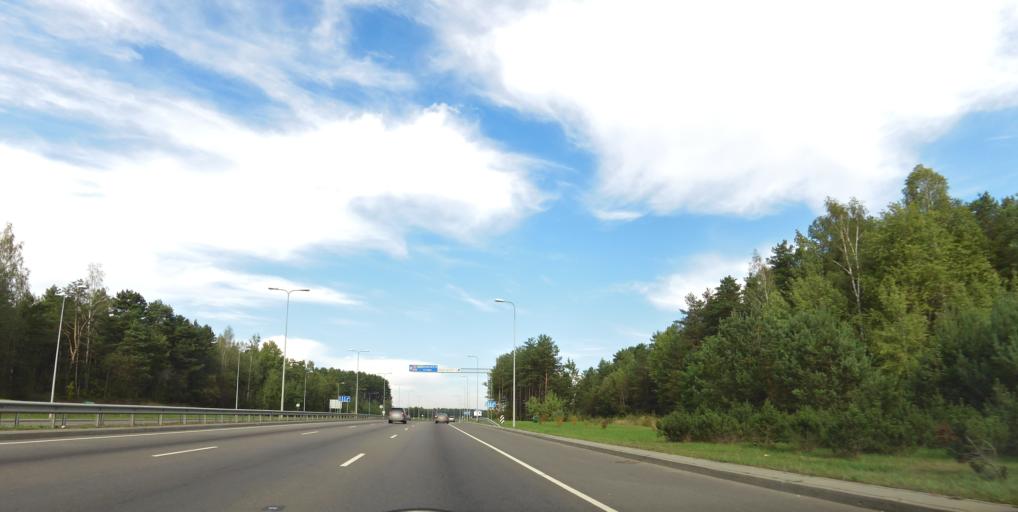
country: LT
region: Vilnius County
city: Lazdynai
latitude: 54.6784
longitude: 25.1954
